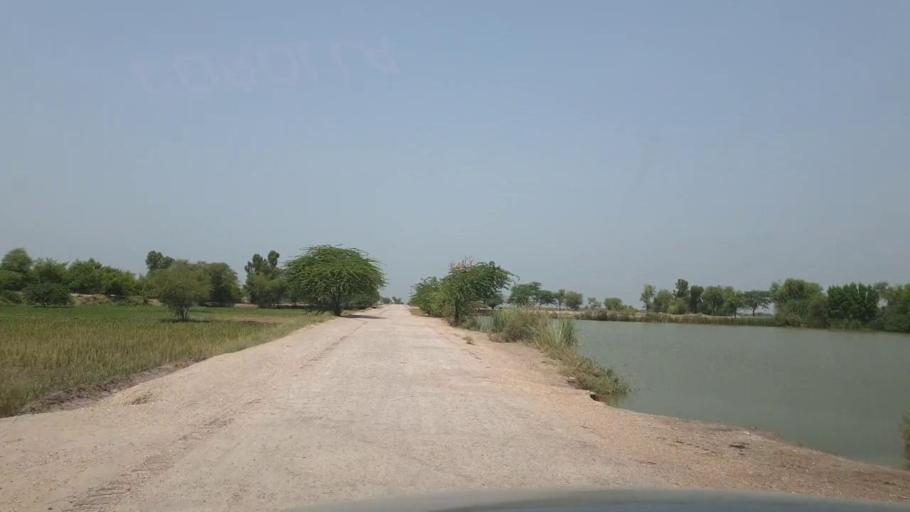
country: PK
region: Sindh
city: Garhi Yasin
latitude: 27.8771
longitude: 68.4456
